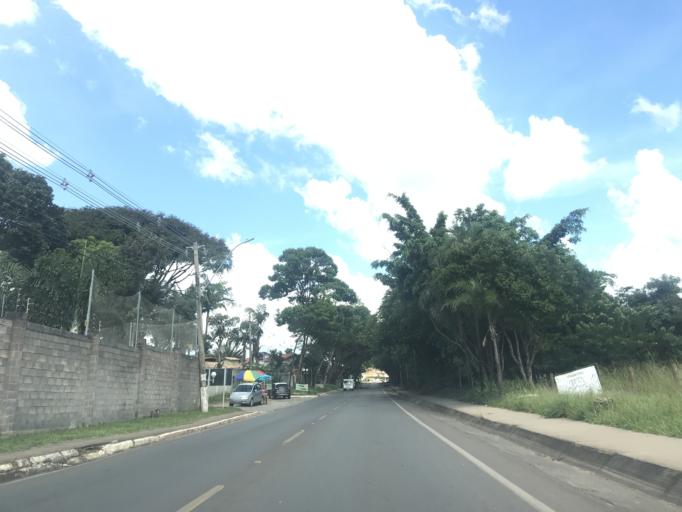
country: BR
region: Federal District
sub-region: Brasilia
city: Brasilia
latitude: -15.8787
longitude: -47.8045
